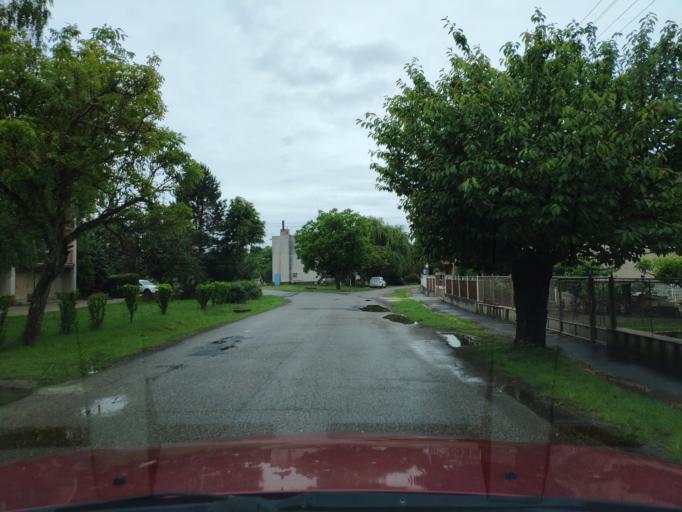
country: HU
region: Borsod-Abauj-Zemplen
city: Karcsa
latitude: 48.3983
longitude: 21.8078
